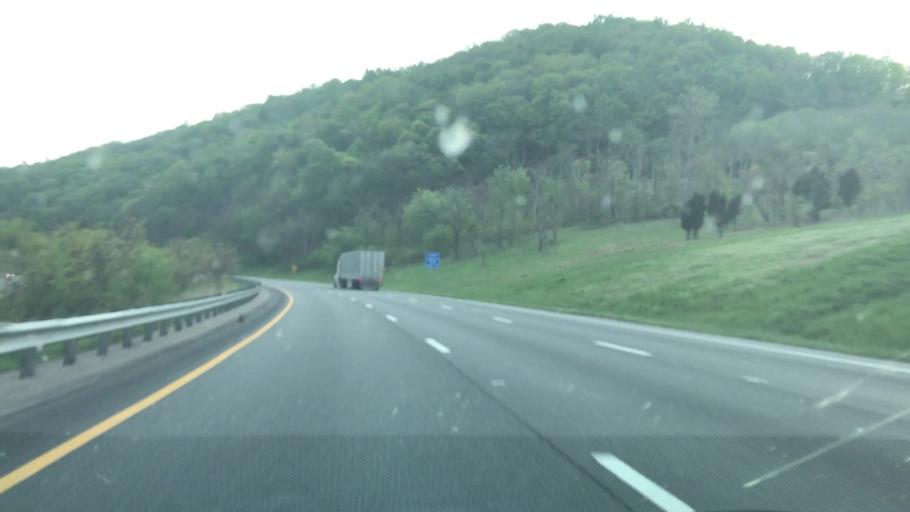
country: US
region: Virginia
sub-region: Montgomery County
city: Shawsville
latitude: 37.2268
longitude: -80.2526
